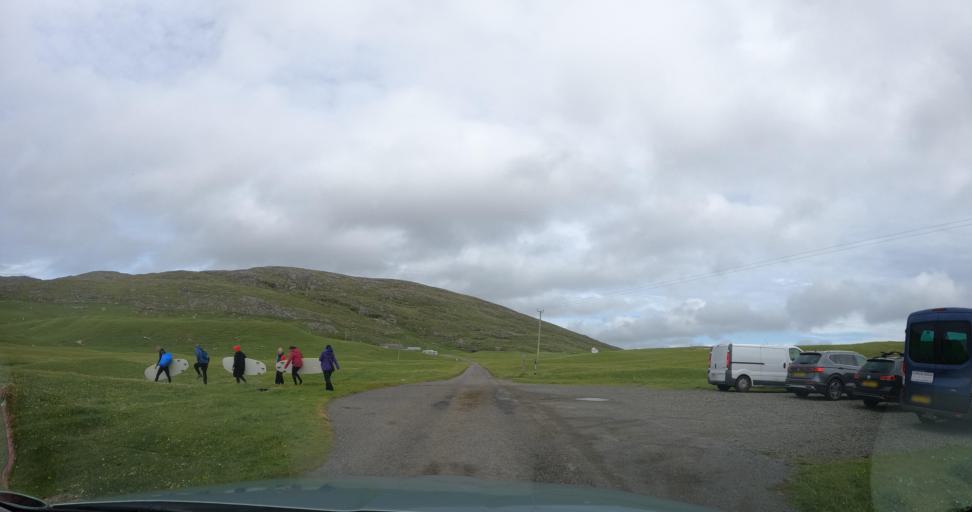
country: GB
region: Scotland
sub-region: Eilean Siar
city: Barra
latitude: 56.9248
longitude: -7.5381
